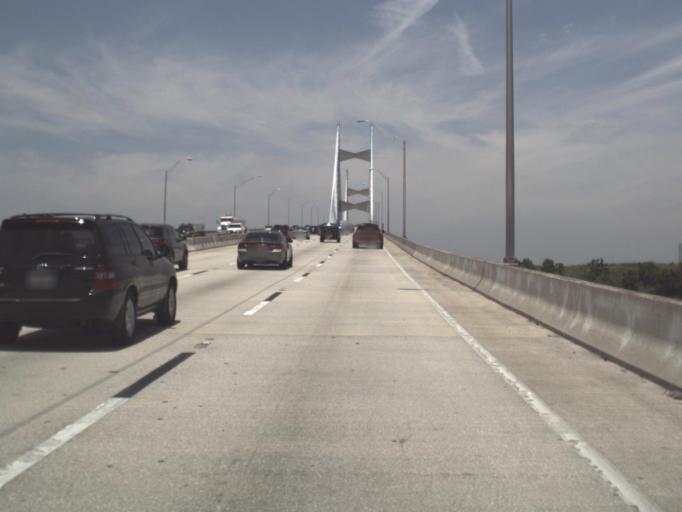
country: US
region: Florida
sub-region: Duval County
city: Jacksonville
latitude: 30.3755
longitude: -81.5529
